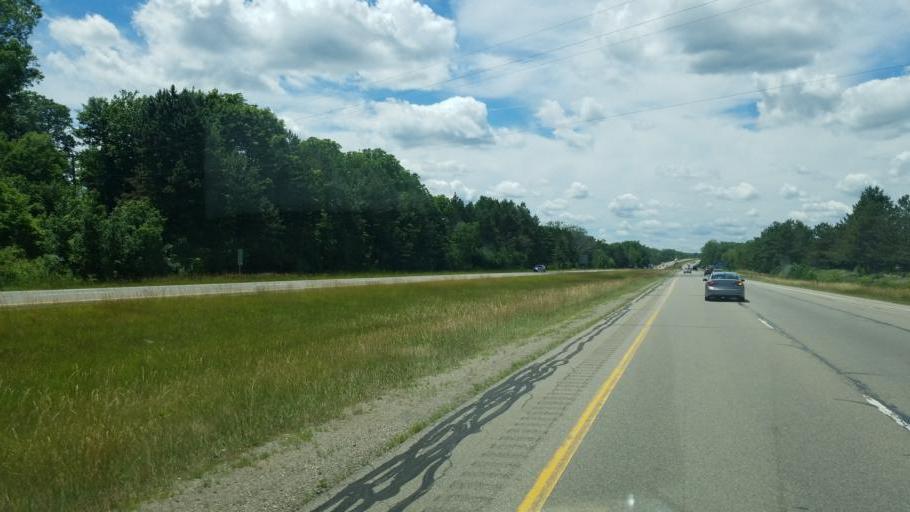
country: US
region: Michigan
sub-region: Ingham County
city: Holt
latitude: 42.6719
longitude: -84.5029
